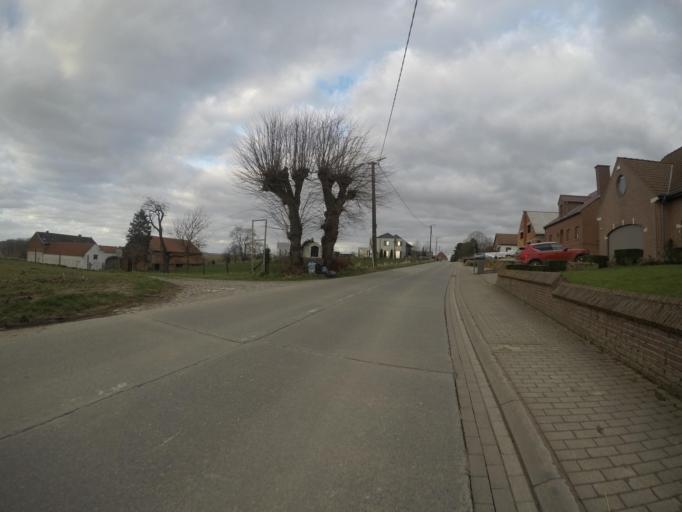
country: BE
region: Flanders
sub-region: Provincie Vlaams-Brabant
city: Pepingen
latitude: 50.7338
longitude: 4.1069
